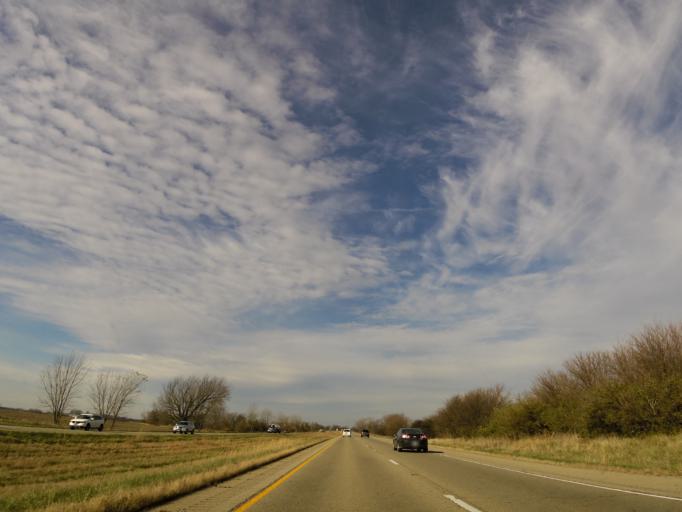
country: US
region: Illinois
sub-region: McLean County
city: Danvers
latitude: 40.6025
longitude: -89.1712
